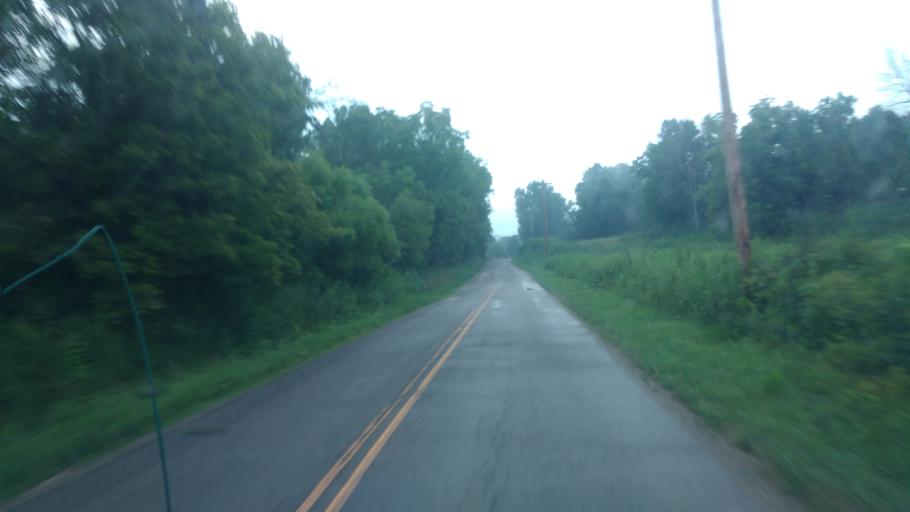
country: US
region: Ohio
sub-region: Guernsey County
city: Byesville
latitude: 40.0419
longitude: -81.3770
